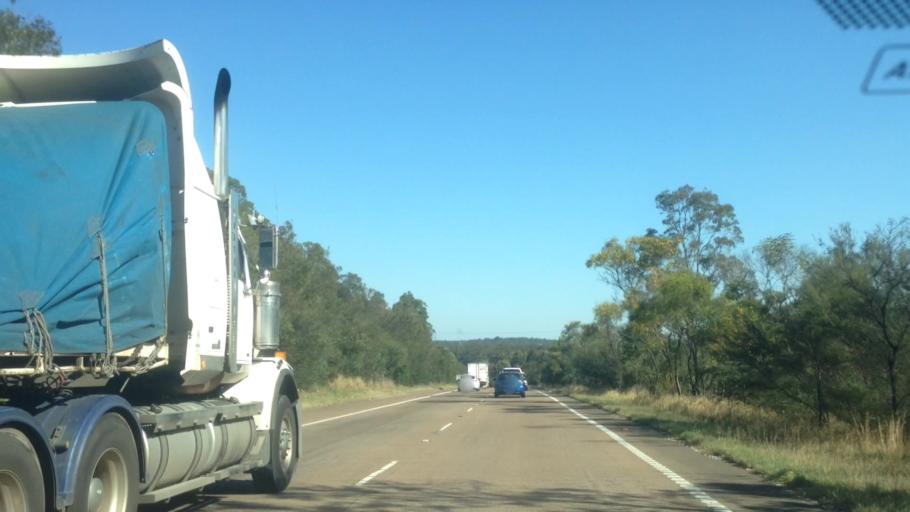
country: AU
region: New South Wales
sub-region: Lake Macquarie Shire
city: Dora Creek
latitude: -33.1519
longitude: 151.4725
